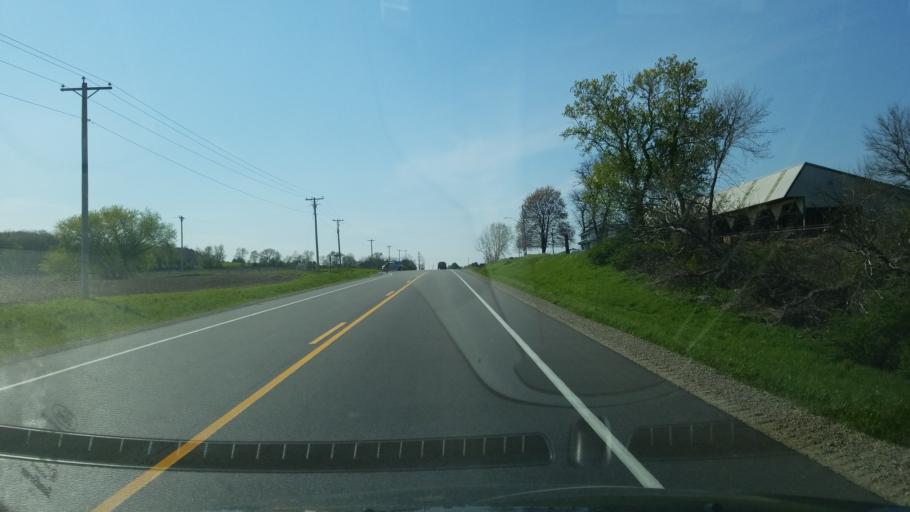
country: US
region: Wisconsin
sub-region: Dane County
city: Fitchburg
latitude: 42.9606
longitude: -89.4795
